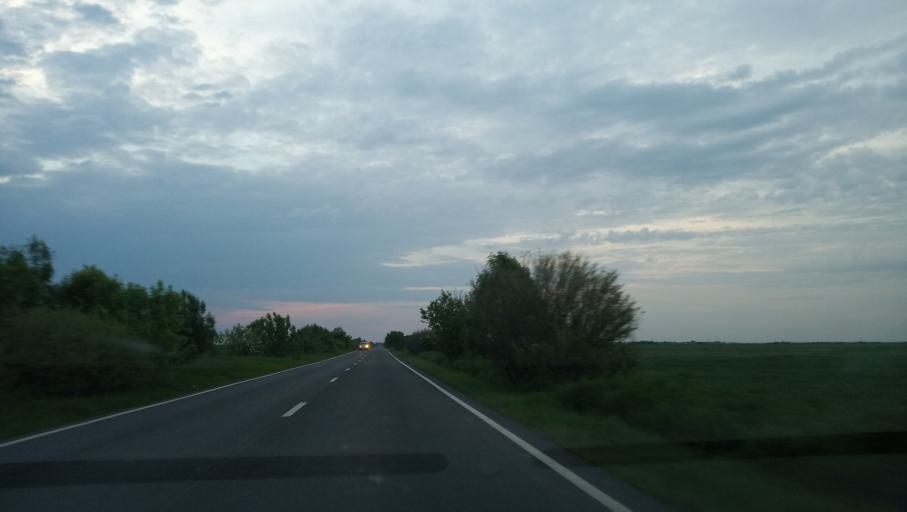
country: RO
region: Timis
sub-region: Comuna Jebel
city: Jebel
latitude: 45.5351
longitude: 21.2282
